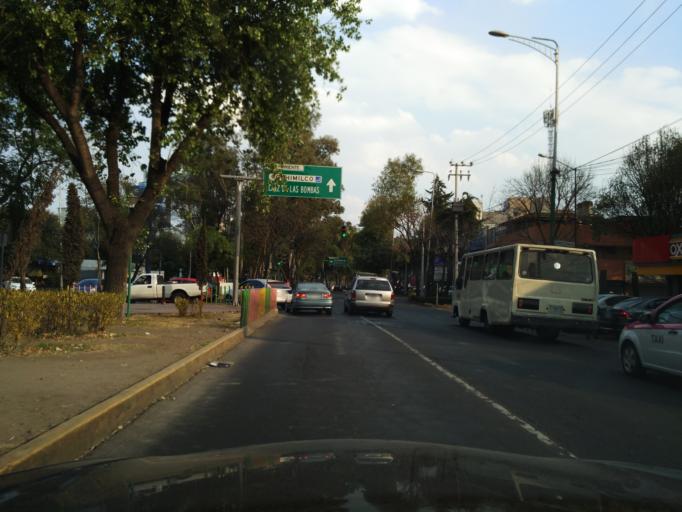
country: MX
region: Mexico City
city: Tlalpan
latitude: 19.3164
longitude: -99.1260
